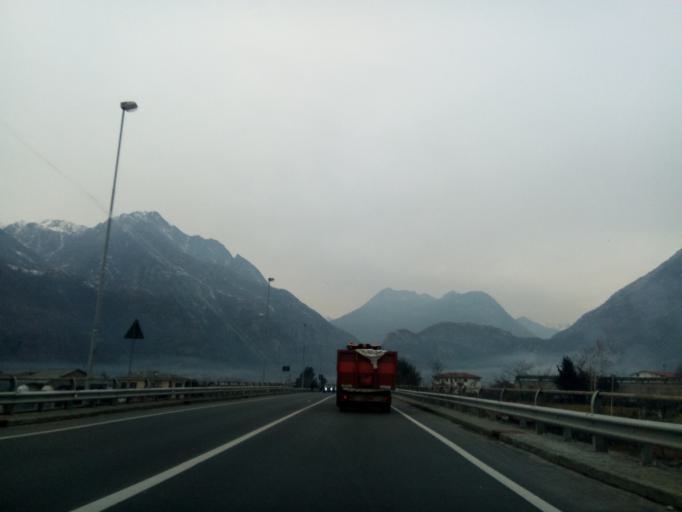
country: IT
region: Aosta Valley
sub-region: Valle d'Aosta
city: Pont-Saint-Martin
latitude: 45.5958
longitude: 7.7956
